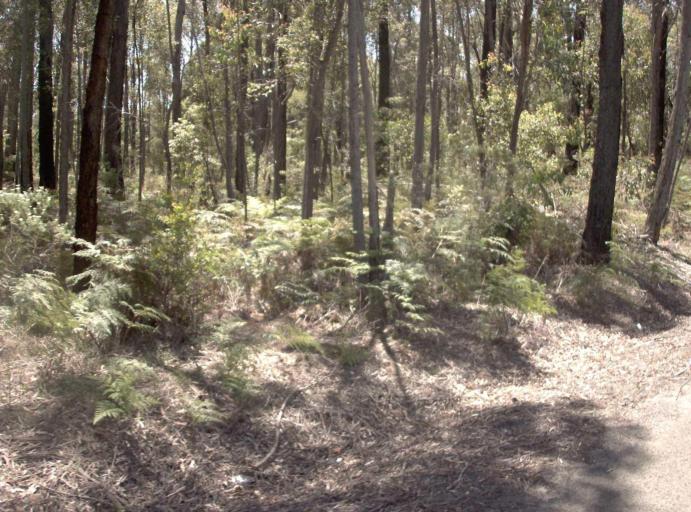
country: AU
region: Victoria
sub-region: East Gippsland
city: Lakes Entrance
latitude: -37.6995
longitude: 148.5872
